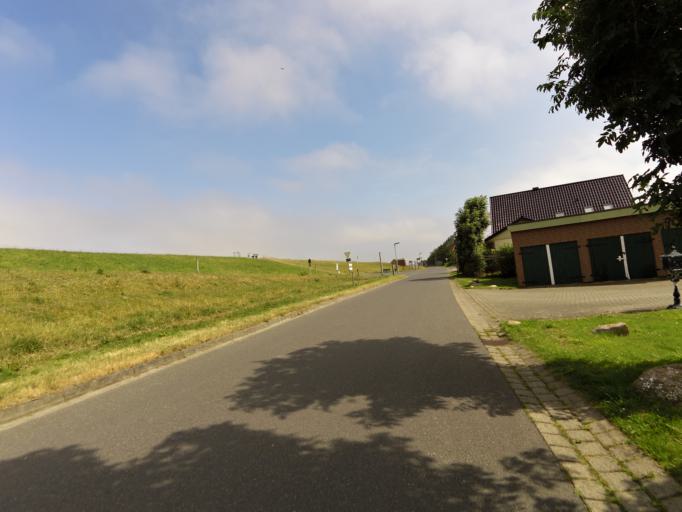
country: DE
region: Lower Saxony
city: Nordholz
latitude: 53.7862
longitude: 8.5525
